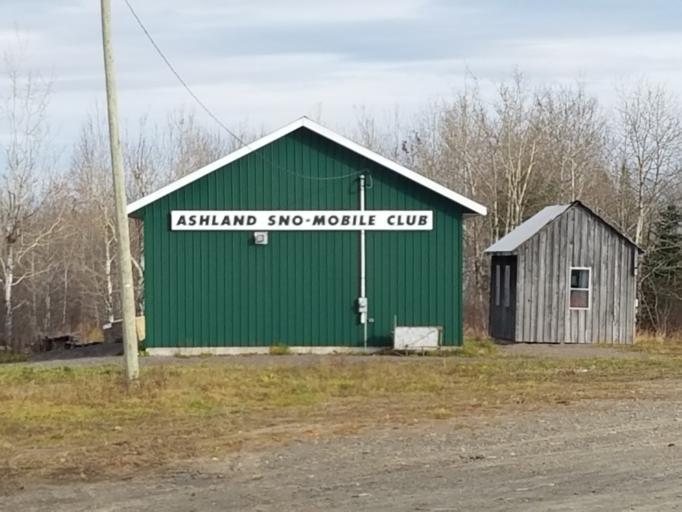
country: US
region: Maine
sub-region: Aroostook County
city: Presque Isle
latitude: 46.6197
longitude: -68.4008
